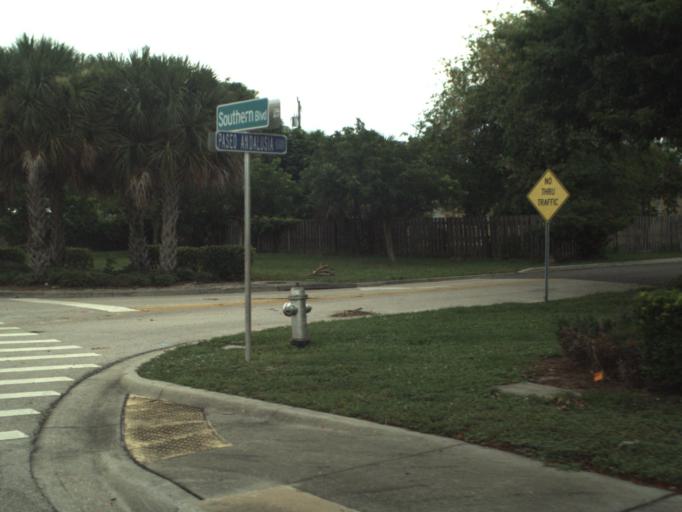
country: US
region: Florida
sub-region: Palm Beach County
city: Lake Clarke Shores
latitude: 26.6762
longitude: -80.0660
